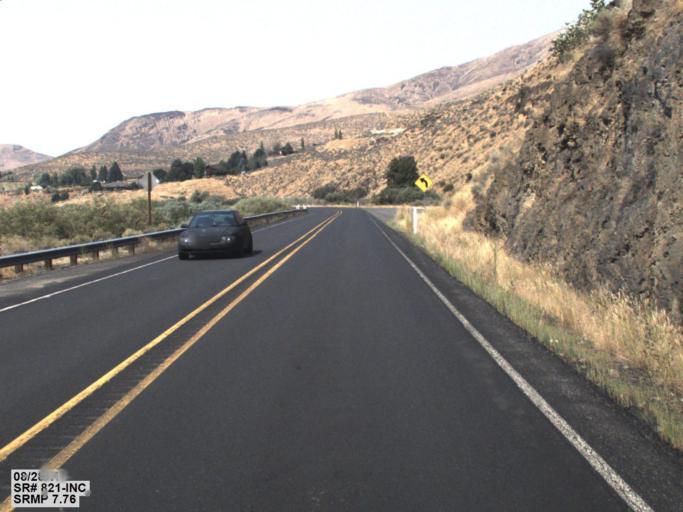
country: US
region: Washington
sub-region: Yakima County
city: Selah
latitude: 46.7700
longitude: -120.4483
